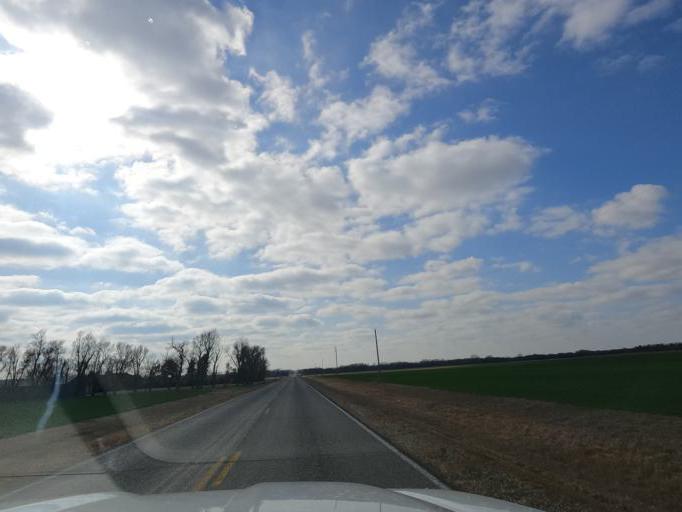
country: US
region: Kansas
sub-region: McPherson County
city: Inman
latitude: 38.2320
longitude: -97.8514
